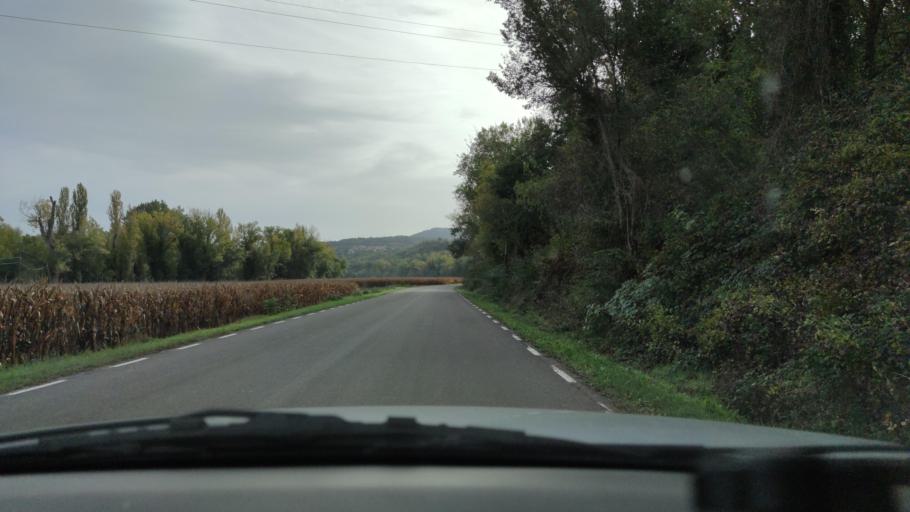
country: ES
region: Catalonia
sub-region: Provincia de Lleida
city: Artesa de Segre
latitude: 41.9186
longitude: 1.0944
